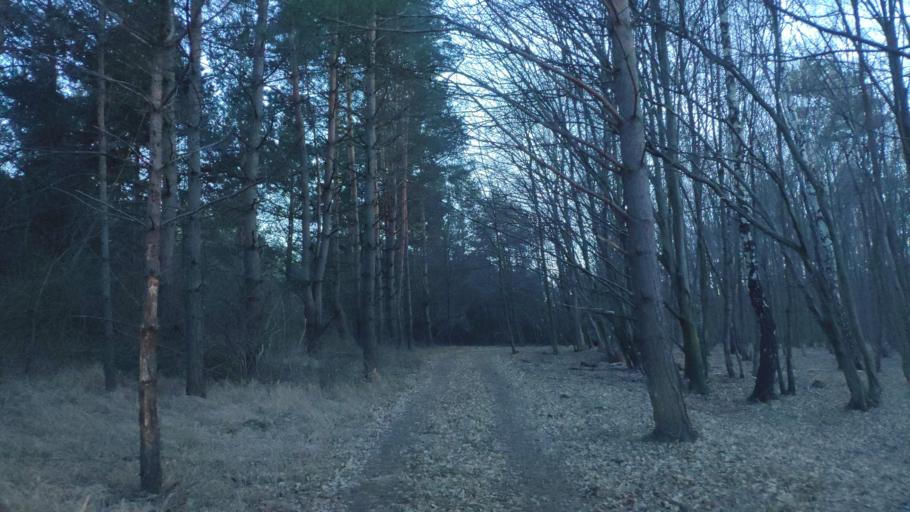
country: SK
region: Kosicky
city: Kosice
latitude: 48.8456
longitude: 21.2449
